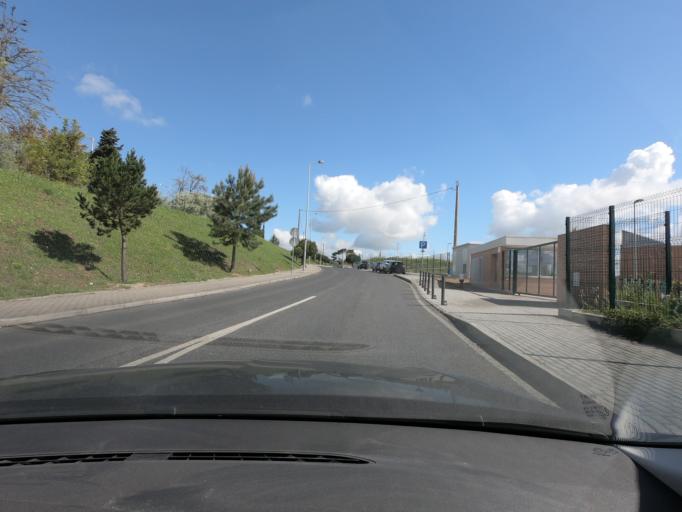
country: PT
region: Lisbon
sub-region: Loures
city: Camarate
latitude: 38.7999
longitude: -9.1353
